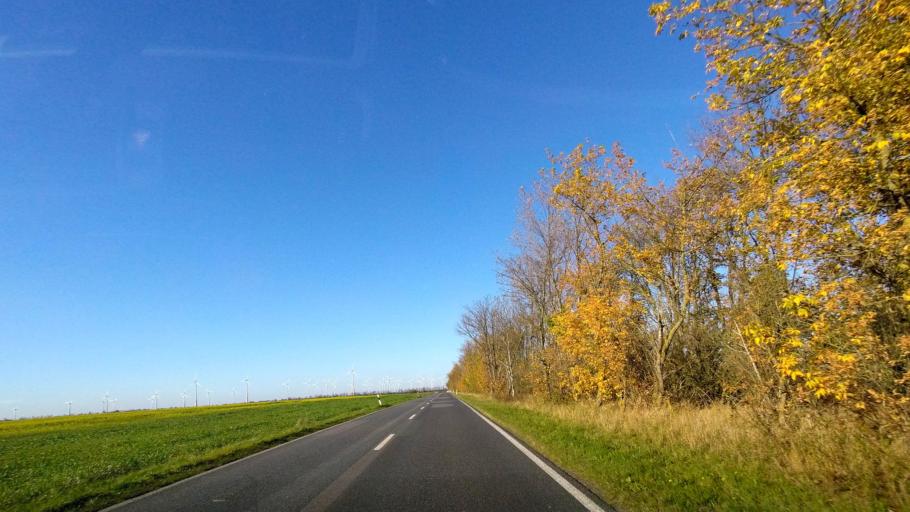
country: DE
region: Saxony-Anhalt
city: Zahna
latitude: 51.9784
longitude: 12.8603
